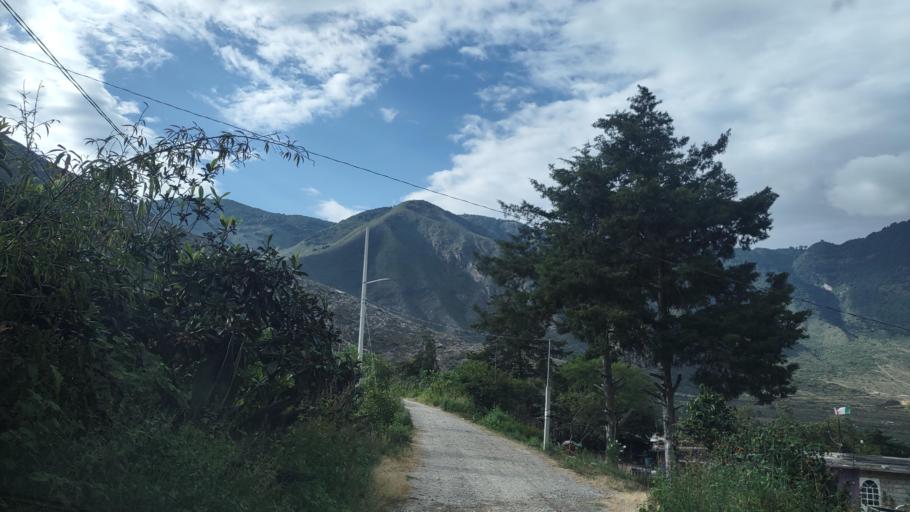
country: MX
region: Veracruz
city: Acultzingo
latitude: 18.7112
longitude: -97.3190
